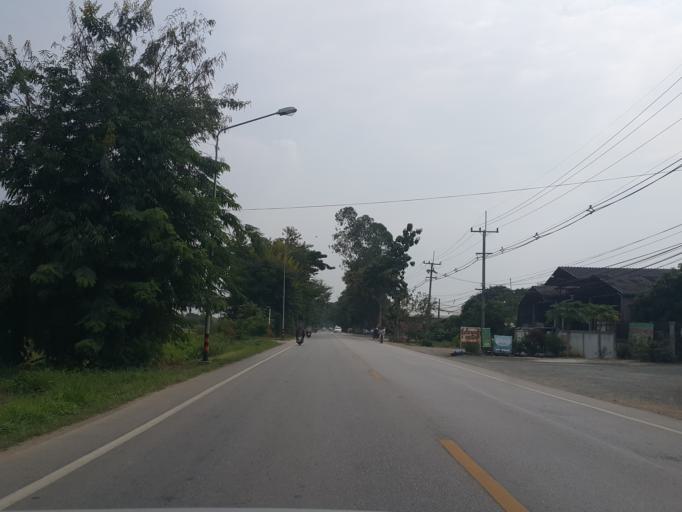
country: TH
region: Chiang Mai
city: Mae Taeng
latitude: 19.0181
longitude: 98.9700
